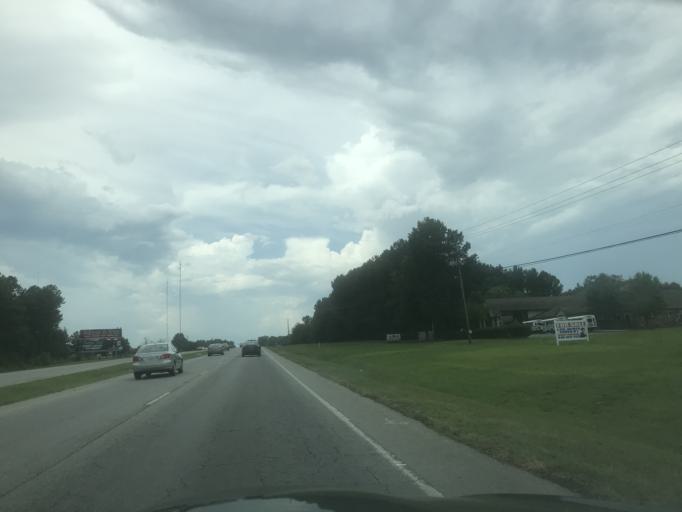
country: US
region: North Carolina
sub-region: Johnston County
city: Clayton
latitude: 35.6625
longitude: -78.4906
